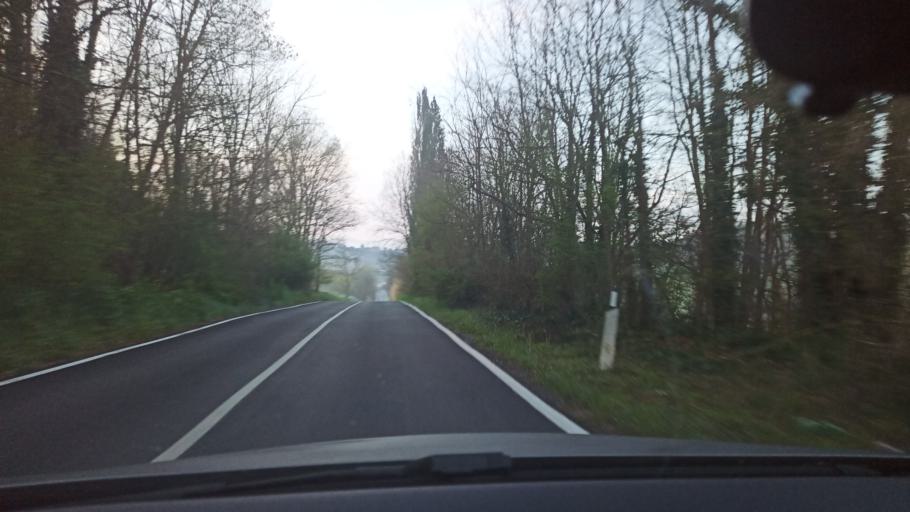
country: IT
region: Latium
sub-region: Provincia di Rieti
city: Cantalupo in Sabina
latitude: 42.3233
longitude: 12.6426
